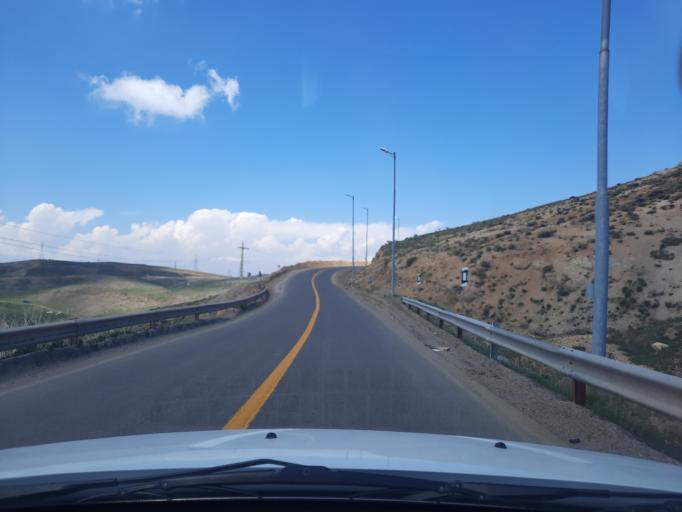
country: IR
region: Qazvin
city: Qazvin
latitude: 36.3865
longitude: 50.2070
